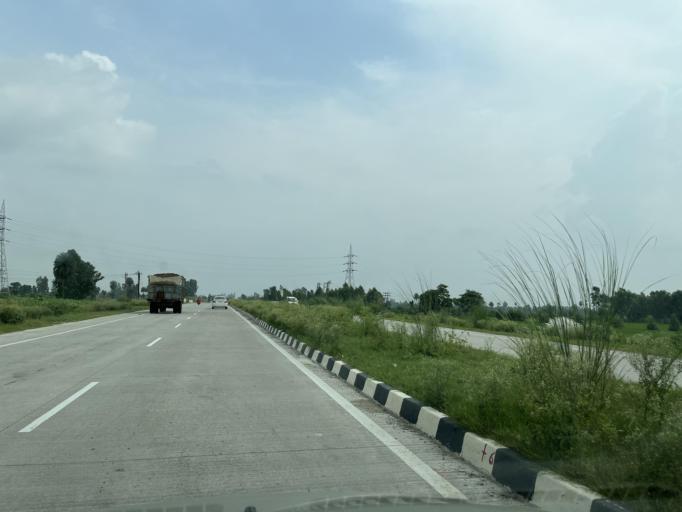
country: IN
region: Uttarakhand
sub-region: Udham Singh Nagar
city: Kashipur
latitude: 29.1686
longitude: 78.9550
